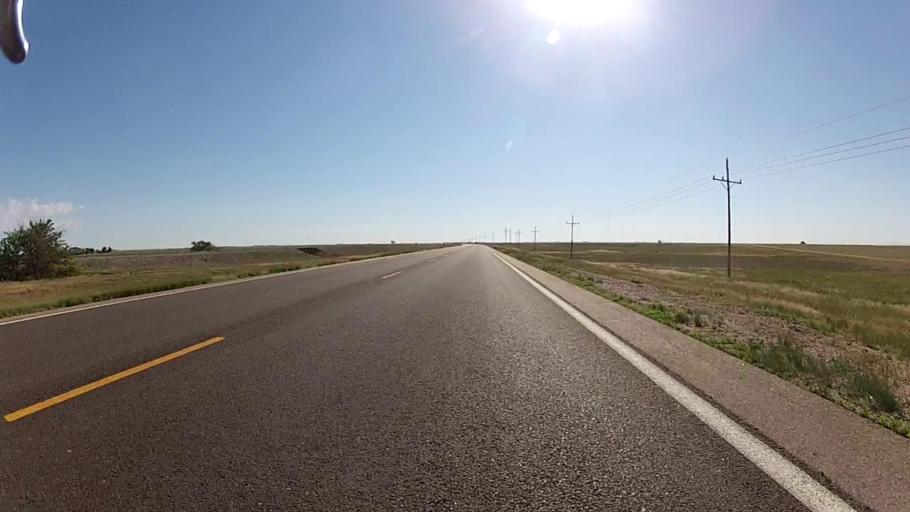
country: US
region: Kansas
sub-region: Haskell County
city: Sublette
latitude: 37.5555
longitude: -100.5834
